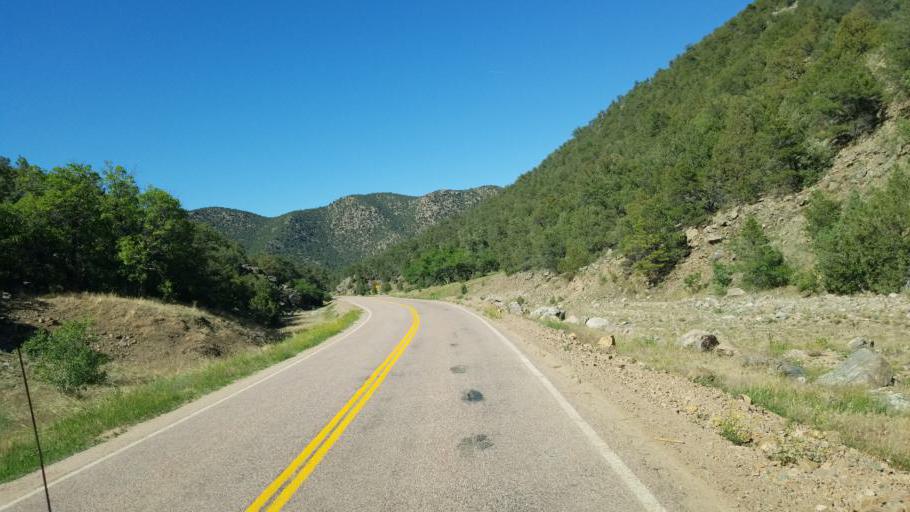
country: US
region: Colorado
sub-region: Fremont County
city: Canon City
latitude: 38.4017
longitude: -105.4414
